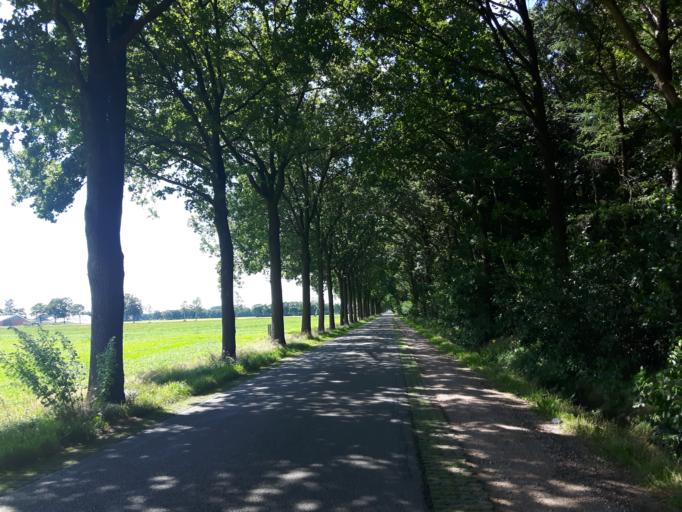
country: NL
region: Overijssel
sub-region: Gemeente Haaksbergen
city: Haaksbergen
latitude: 52.1806
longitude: 6.7612
